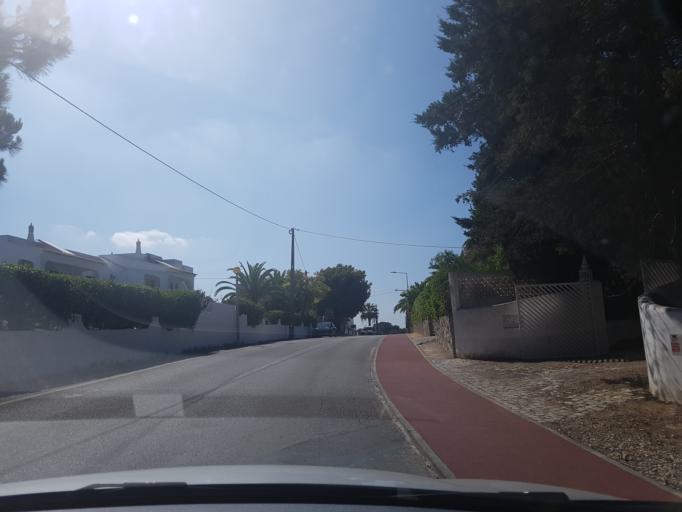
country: PT
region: Faro
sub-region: Lagoa
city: Carvoeiro
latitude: 37.0927
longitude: -8.4455
